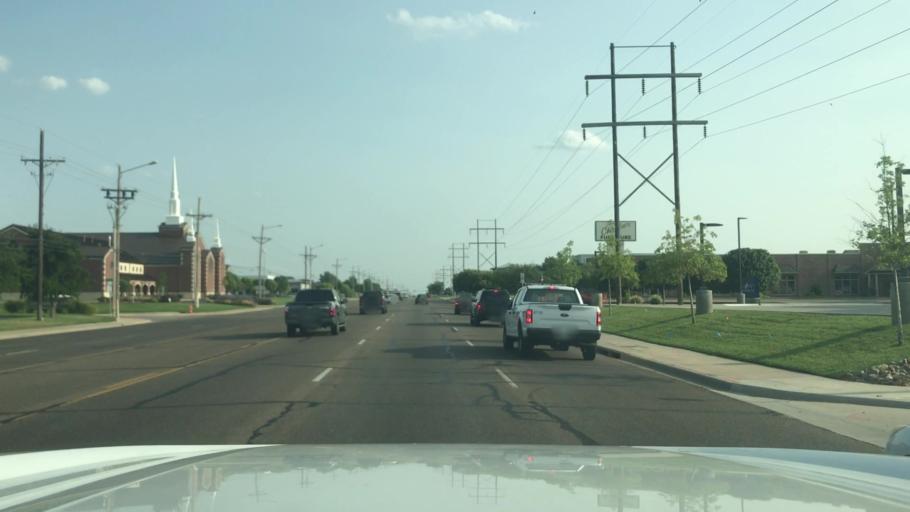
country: US
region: Texas
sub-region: Potter County
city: Amarillo
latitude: 35.1690
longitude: -101.9382
